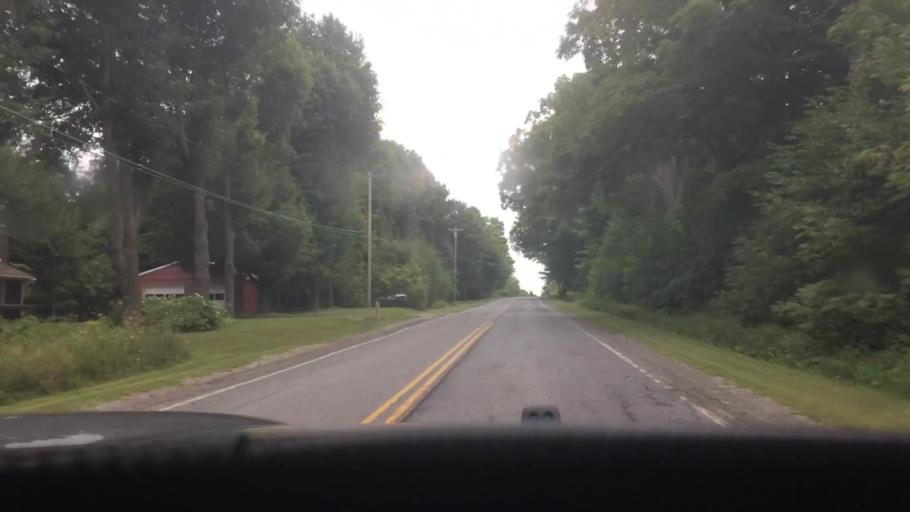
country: US
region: New York
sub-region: St. Lawrence County
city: Hannawa Falls
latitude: 44.6158
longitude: -74.8686
